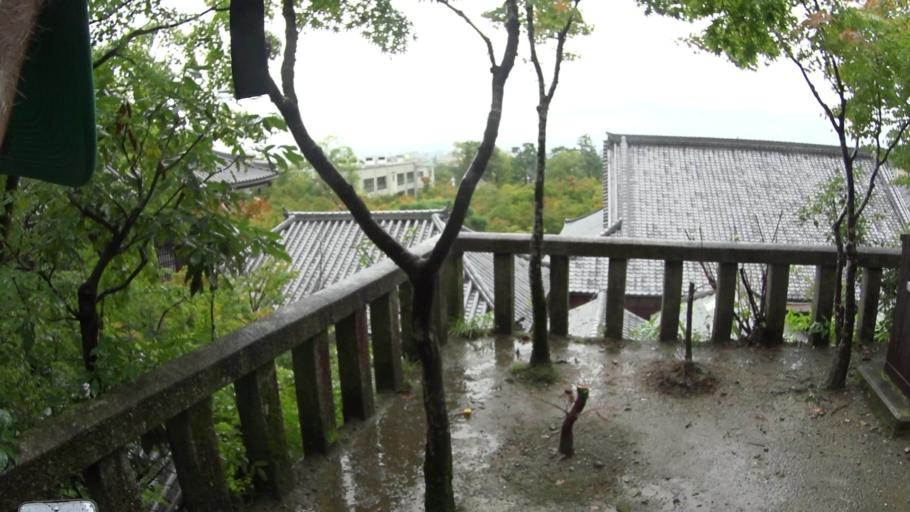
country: JP
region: Shiga Prefecture
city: Otsu-shi
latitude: 34.9800
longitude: 135.8111
